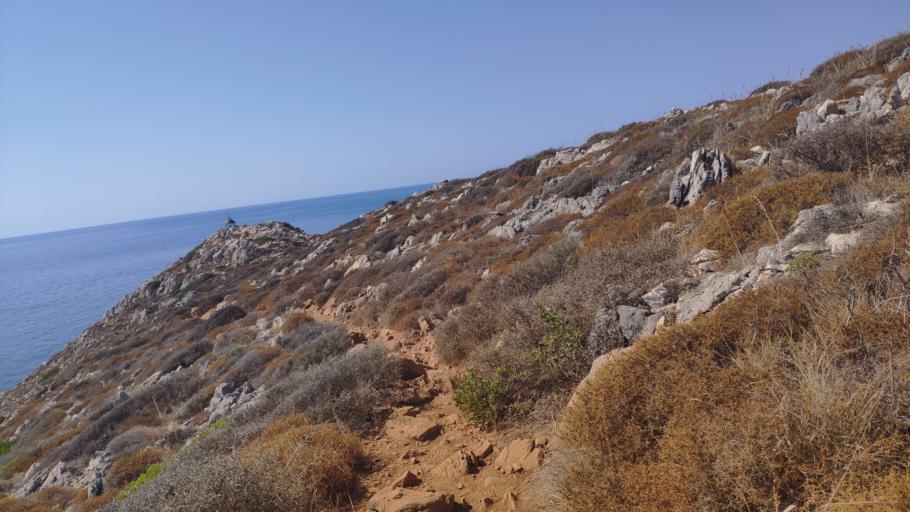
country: GR
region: Peloponnese
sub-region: Nomos Lakonias
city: Gytheio
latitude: 36.3879
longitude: 22.4828
